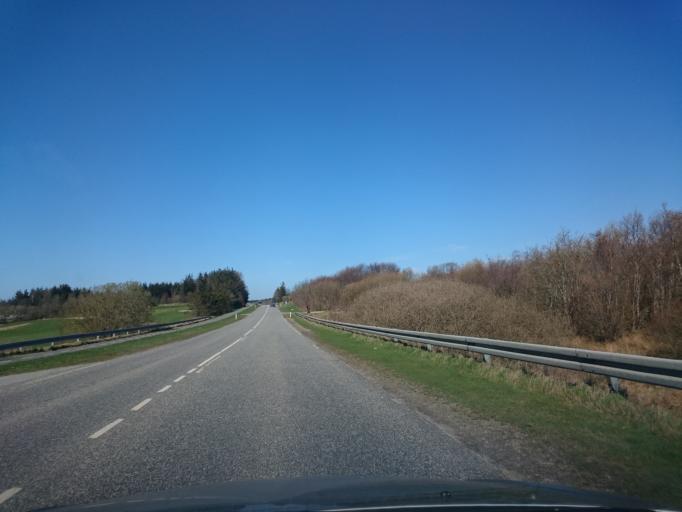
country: DK
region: North Denmark
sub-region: Hjorring Kommune
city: Hjorring
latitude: 57.4933
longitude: 10.0018
